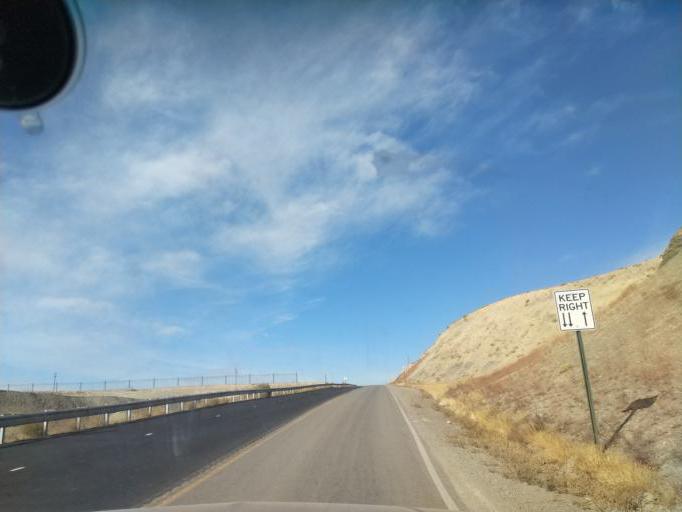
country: US
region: Colorado
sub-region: Mesa County
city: Fruitvale
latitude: 39.0117
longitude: -108.4844
